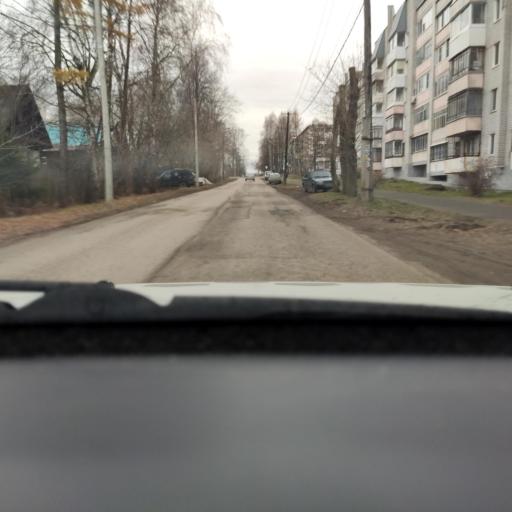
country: RU
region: Perm
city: Polazna
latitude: 58.1294
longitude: 56.3903
